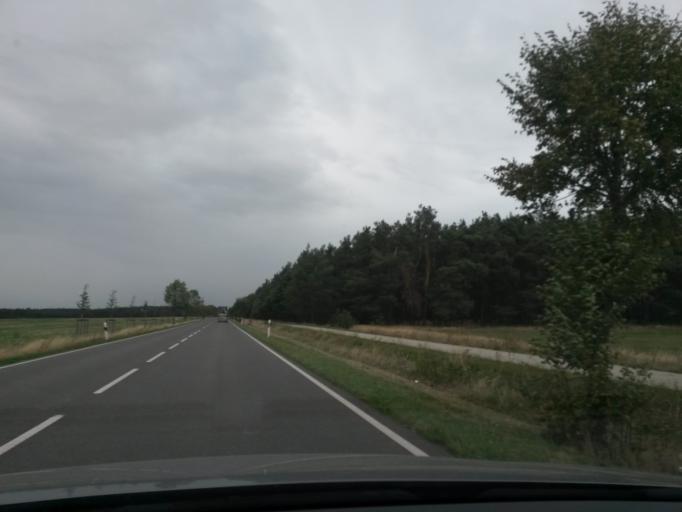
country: DE
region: Saxony-Anhalt
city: Klietz
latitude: 52.7055
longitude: 12.0689
